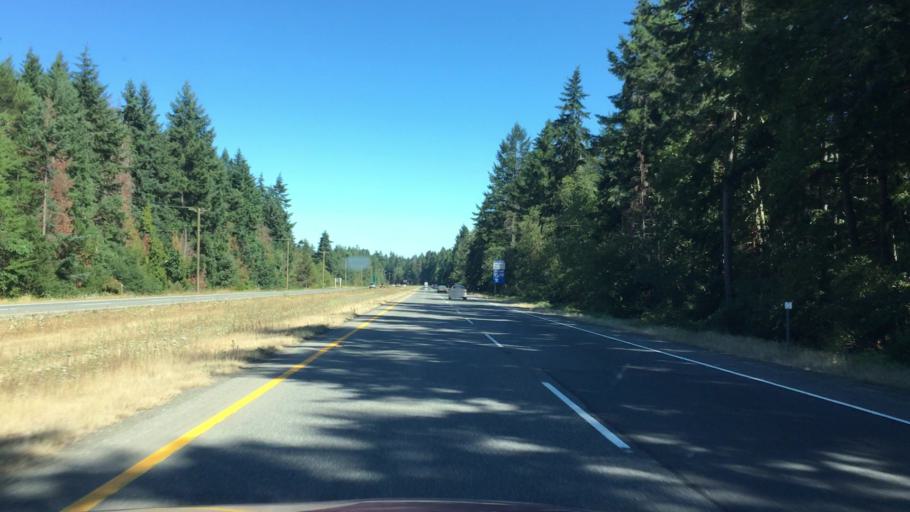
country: CA
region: British Columbia
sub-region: Regional District of Nanaimo
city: Parksville
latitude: 49.3004
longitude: -124.2929
